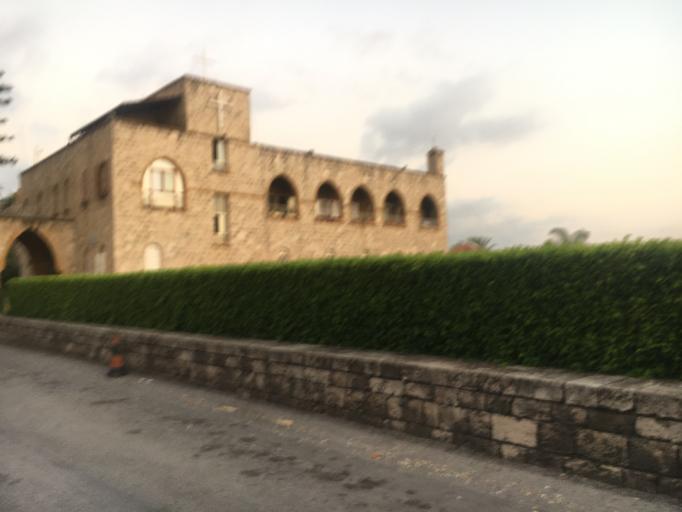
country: LB
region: Mont-Liban
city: Jbail
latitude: 34.1216
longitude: 35.6455
